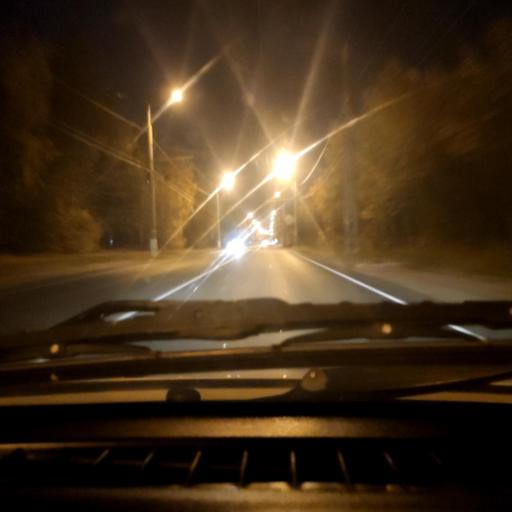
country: RU
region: Samara
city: Tol'yatti
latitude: 53.4901
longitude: 49.3849
